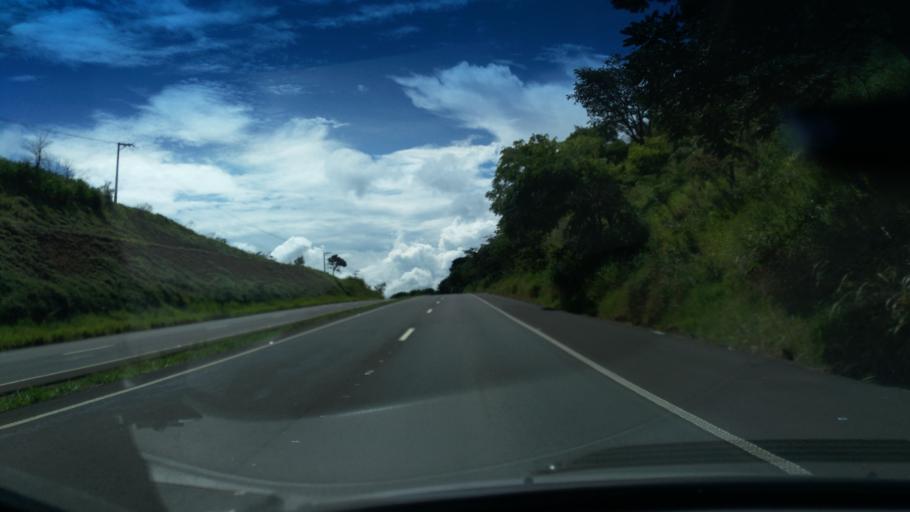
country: BR
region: Sao Paulo
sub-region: Santo Antonio Do Jardim
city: Espirito Santo do Pinhal
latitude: -22.1798
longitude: -46.7548
